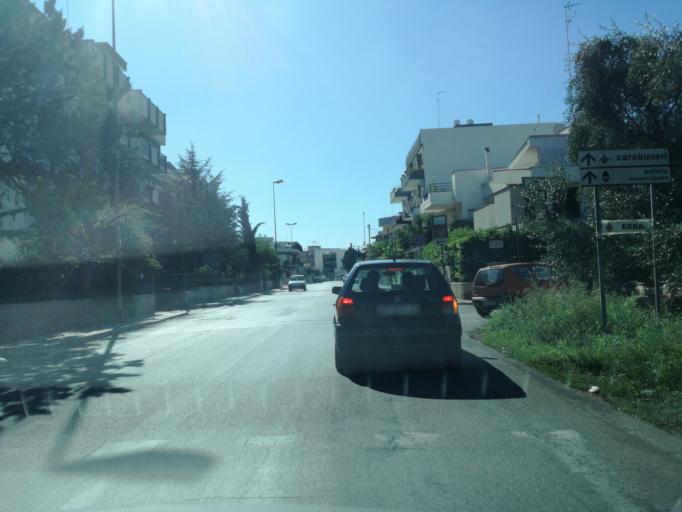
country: IT
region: Apulia
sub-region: Provincia di Bari
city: Capurso
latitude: 41.0517
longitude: 16.9169
